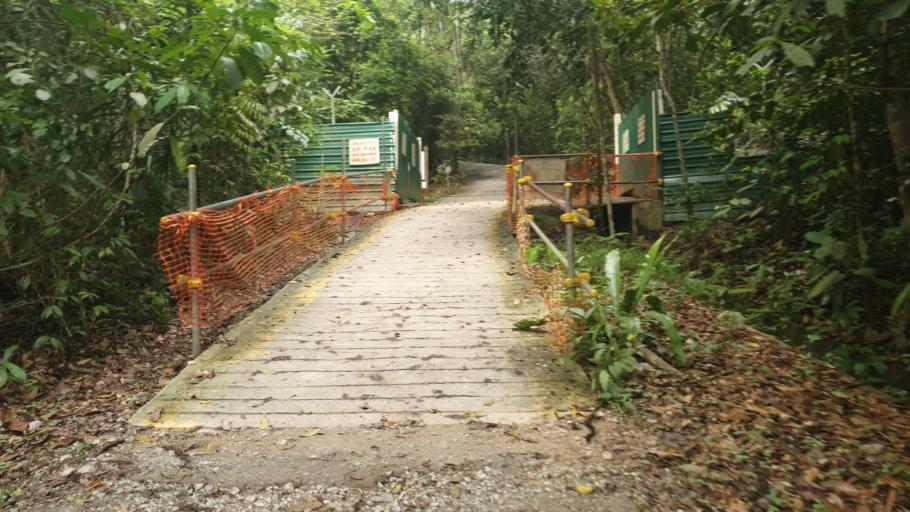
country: SG
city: Singapore
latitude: 1.3584
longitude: 103.8120
